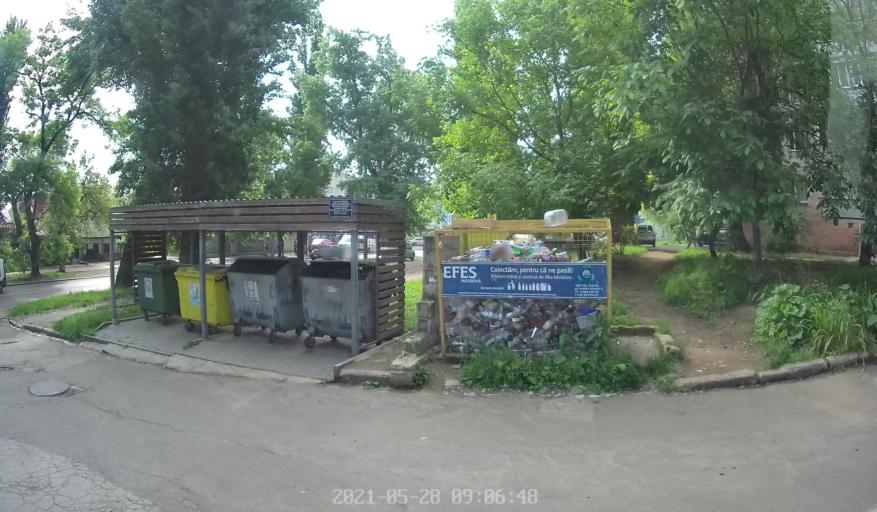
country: MD
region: Chisinau
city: Chisinau
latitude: 47.0024
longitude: 28.8694
